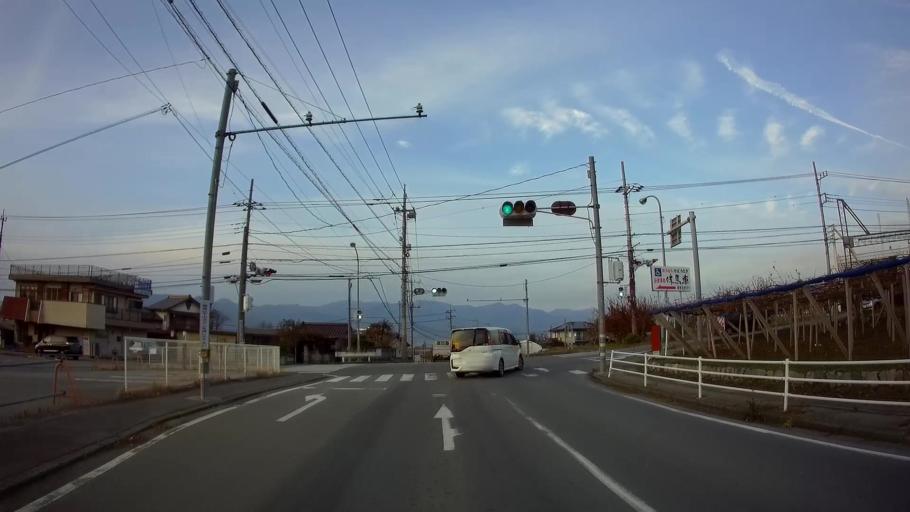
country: JP
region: Yamanashi
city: Isawa
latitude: 35.6200
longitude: 138.6764
